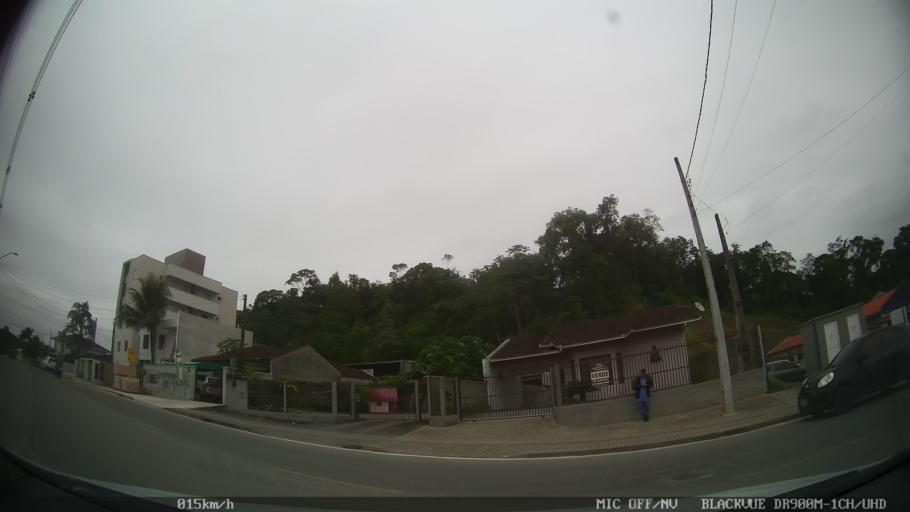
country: BR
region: Santa Catarina
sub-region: Joinville
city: Joinville
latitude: -26.2773
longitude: -48.9027
